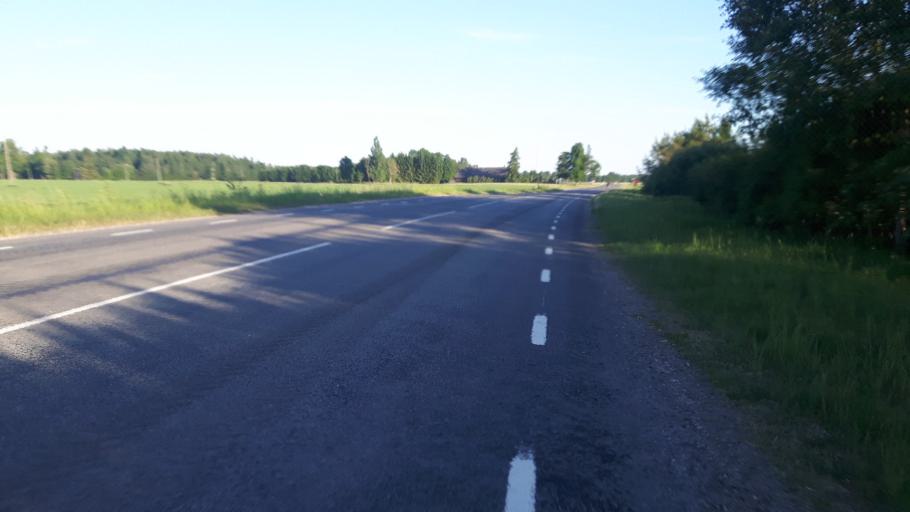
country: EE
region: Raplamaa
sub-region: Jaervakandi vald
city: Jarvakandi
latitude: 58.7799
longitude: 24.9437
